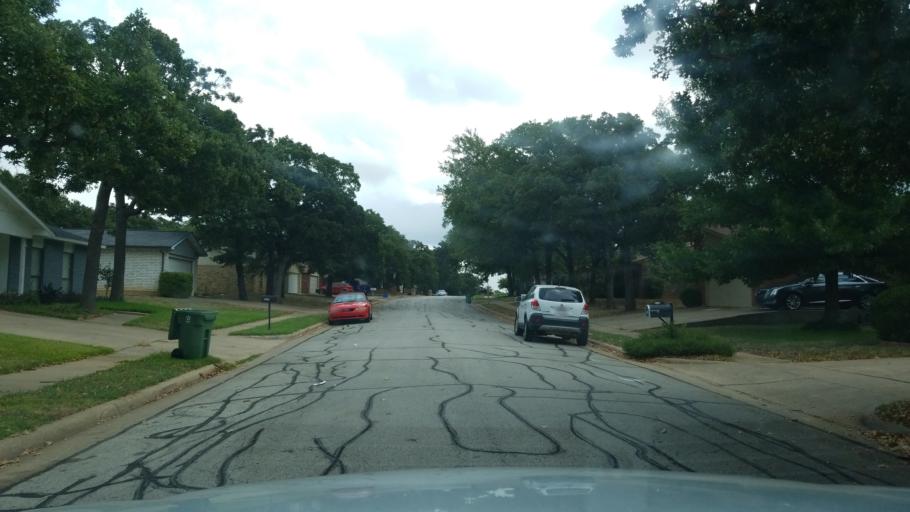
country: US
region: Texas
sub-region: Tarrant County
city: Euless
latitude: 32.8458
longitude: -97.1079
